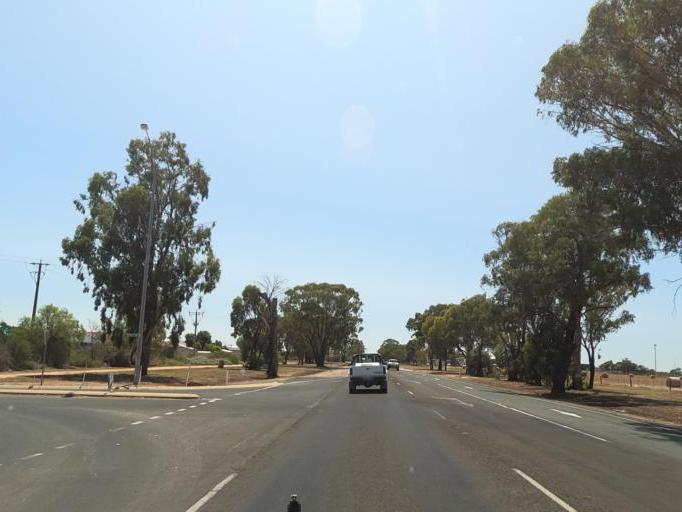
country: AU
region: Victoria
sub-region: Moira
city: Yarrawonga
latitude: -36.0128
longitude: 146.0206
